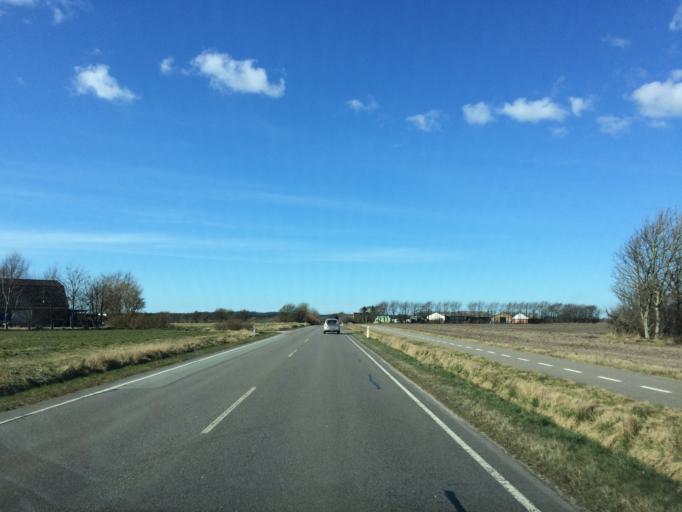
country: DK
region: South Denmark
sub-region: Varde Kommune
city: Oksbol
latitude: 55.7169
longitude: 8.2953
